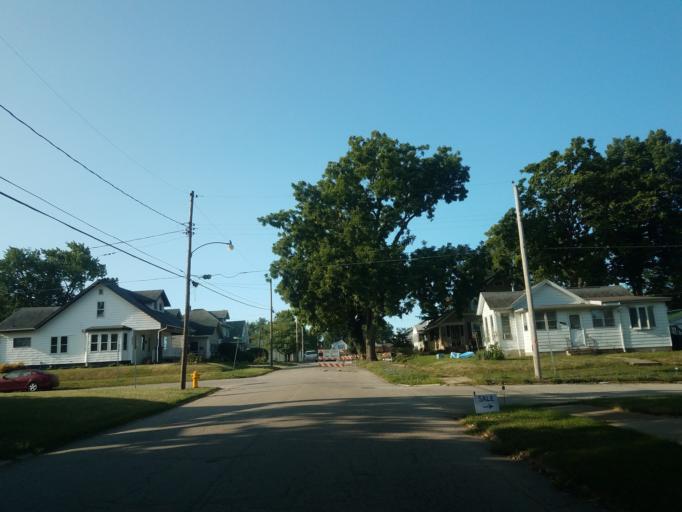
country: US
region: Illinois
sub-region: McLean County
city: Bloomington
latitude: 40.4757
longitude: -88.9780
